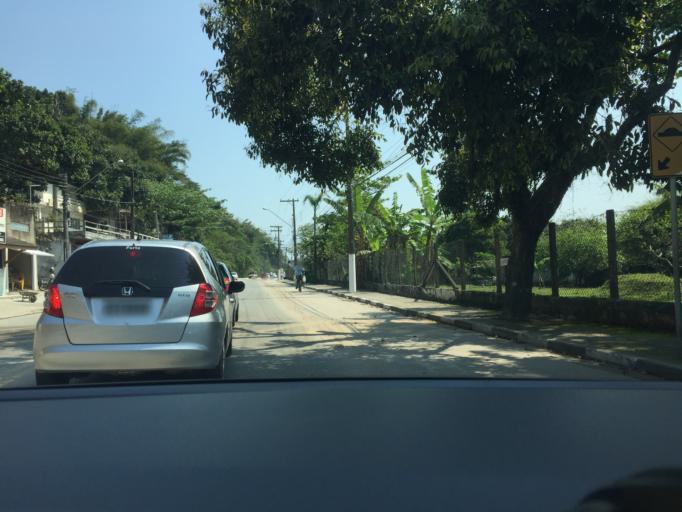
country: BR
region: Sao Paulo
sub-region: Guaruja
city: Guaruja
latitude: -23.9800
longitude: -46.1928
